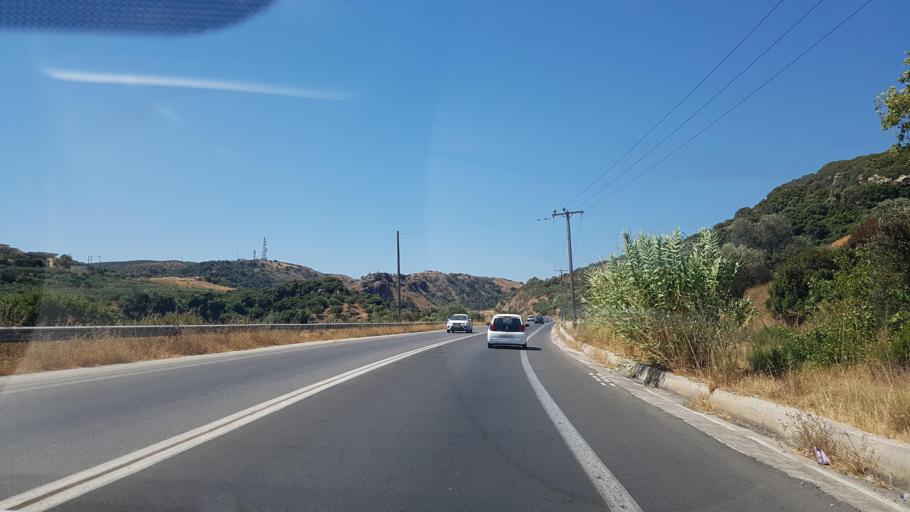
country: GR
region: Crete
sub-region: Nomos Chanias
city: Kolympari
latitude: 35.5221
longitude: 23.7466
